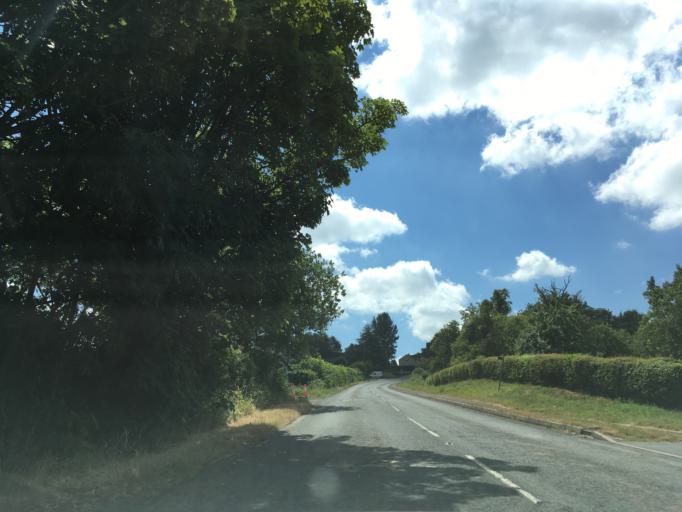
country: GB
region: England
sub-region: Gloucestershire
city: Barnwood
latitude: 51.8290
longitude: -2.2057
